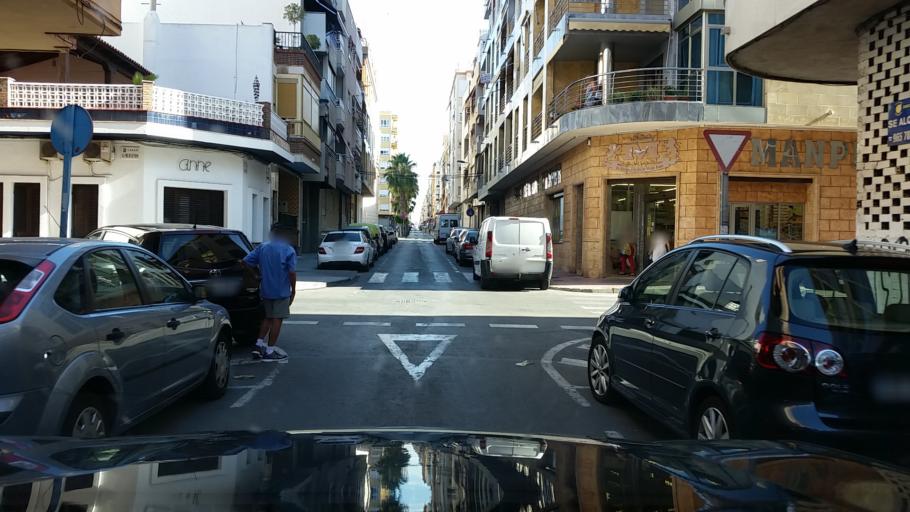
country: ES
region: Valencia
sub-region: Provincia de Alicante
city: Torrevieja
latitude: 37.9754
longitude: -0.6761
